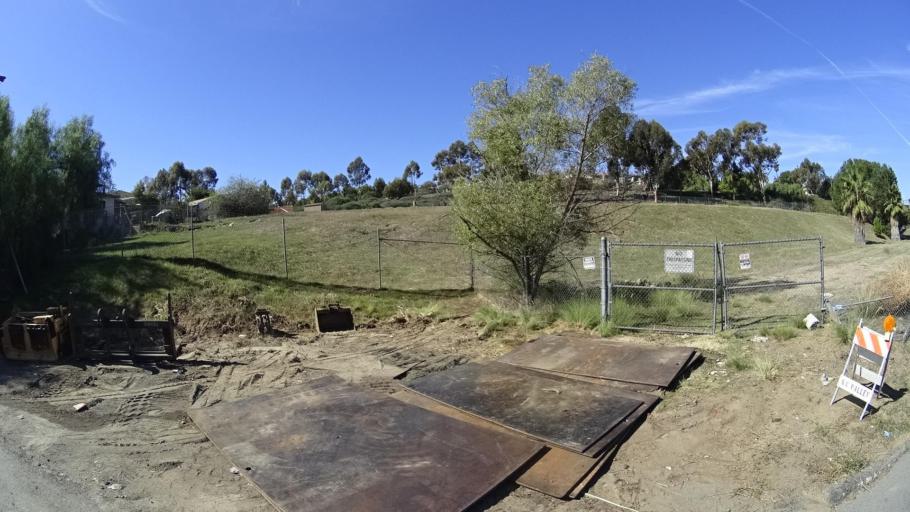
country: US
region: California
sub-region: San Diego County
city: Spring Valley
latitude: 32.7411
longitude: -117.0146
